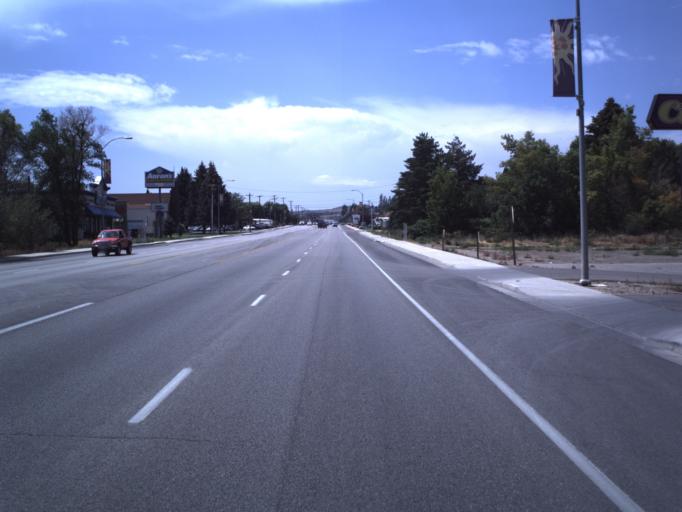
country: US
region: Utah
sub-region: Uintah County
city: Vernal
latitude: 40.4470
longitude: -109.5550
